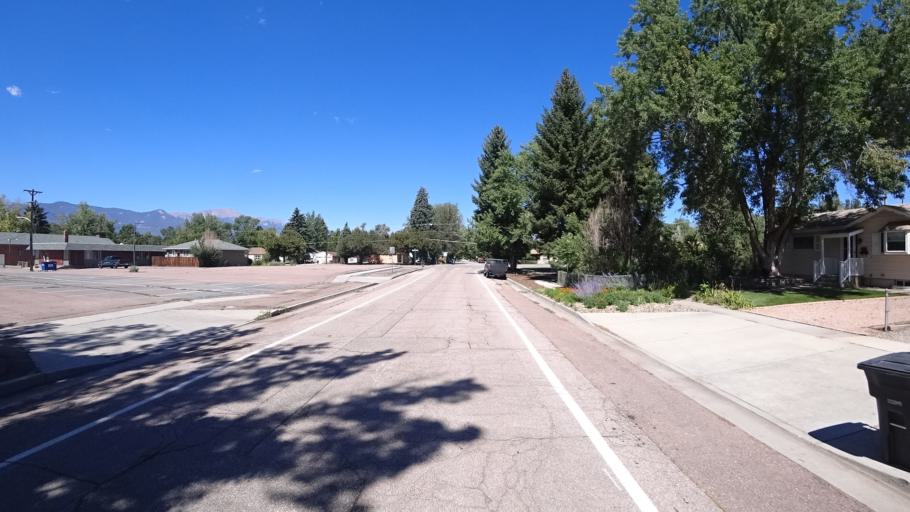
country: US
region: Colorado
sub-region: El Paso County
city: Colorado Springs
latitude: 38.8661
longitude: -104.8067
